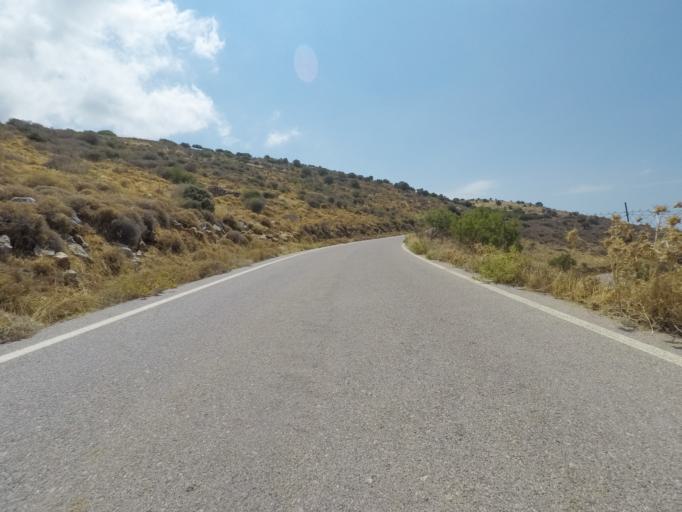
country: GR
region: Crete
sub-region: Nomos Lasithiou
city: Elounda
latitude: 35.3180
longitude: 25.6781
